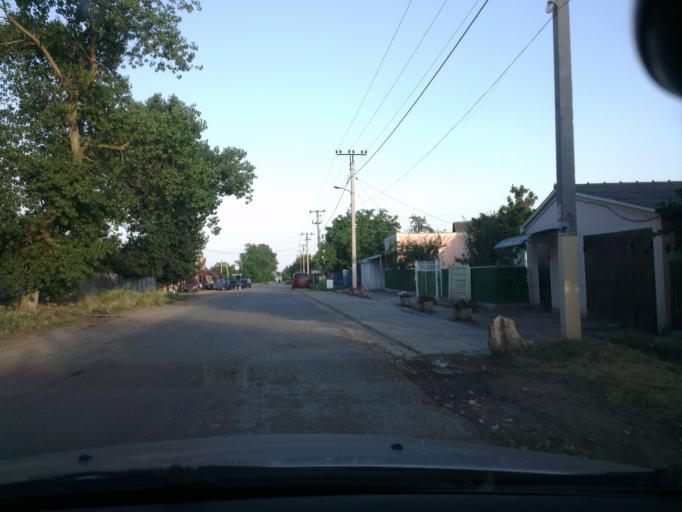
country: MD
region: Cantemir
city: Visniovca
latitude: 46.3518
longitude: 28.4115
